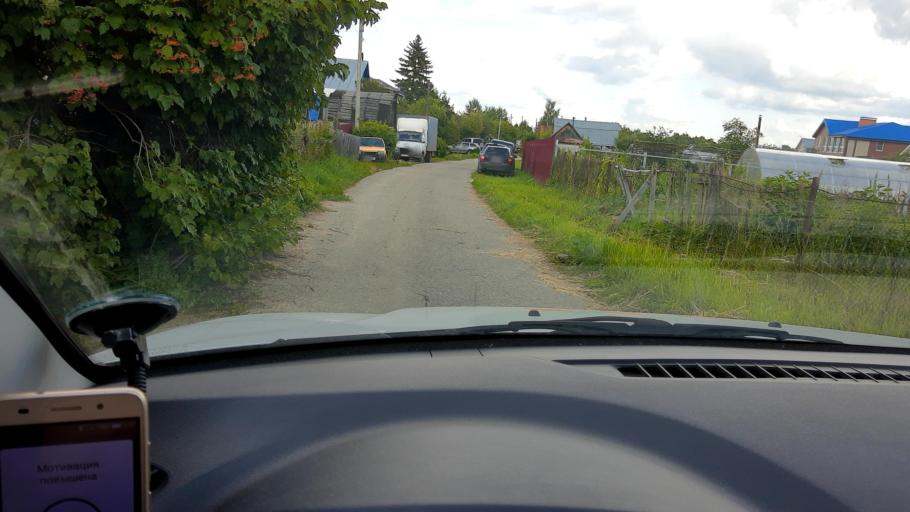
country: RU
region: Nizjnij Novgorod
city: Afonino
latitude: 56.2006
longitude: 44.0316
